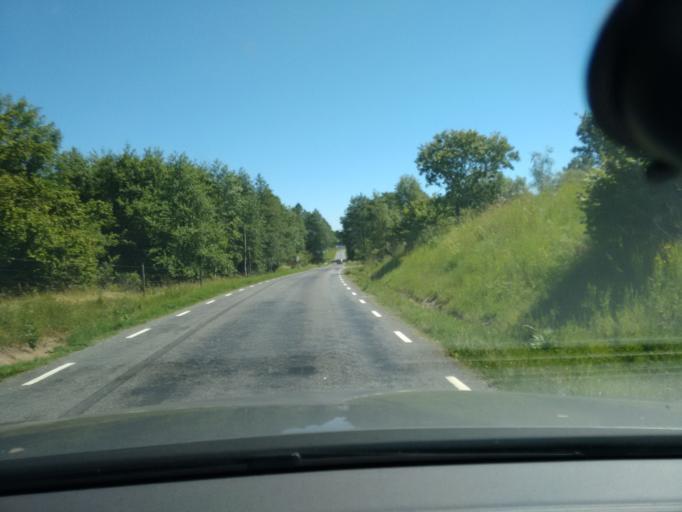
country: SE
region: Skane
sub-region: Kristianstads Kommun
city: Degeberga
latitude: 55.7810
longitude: 14.0722
